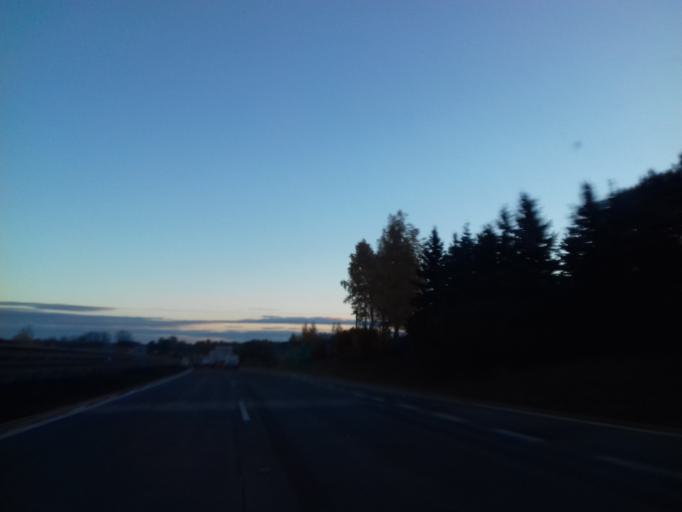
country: CZ
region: South Moravian
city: Rousinov
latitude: 49.1908
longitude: 16.8828
